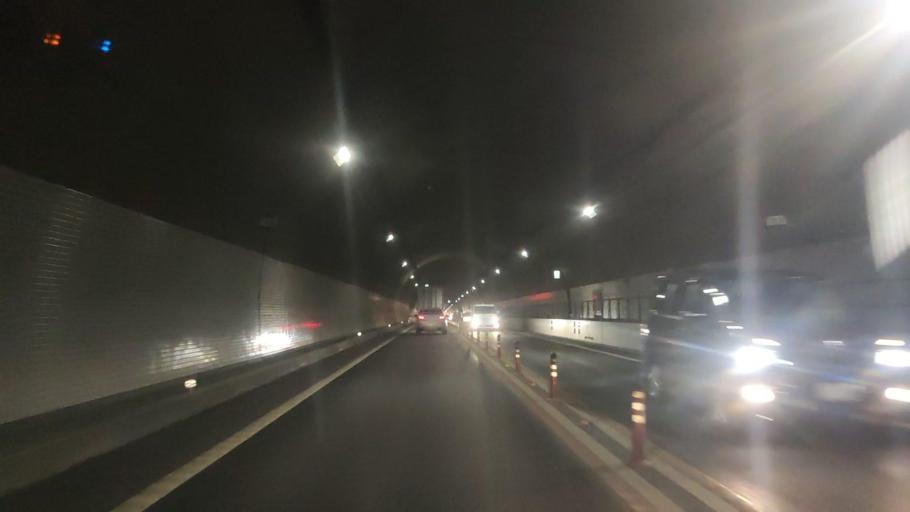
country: JP
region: Fukuoka
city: Kanda
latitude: 33.7640
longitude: 130.9628
